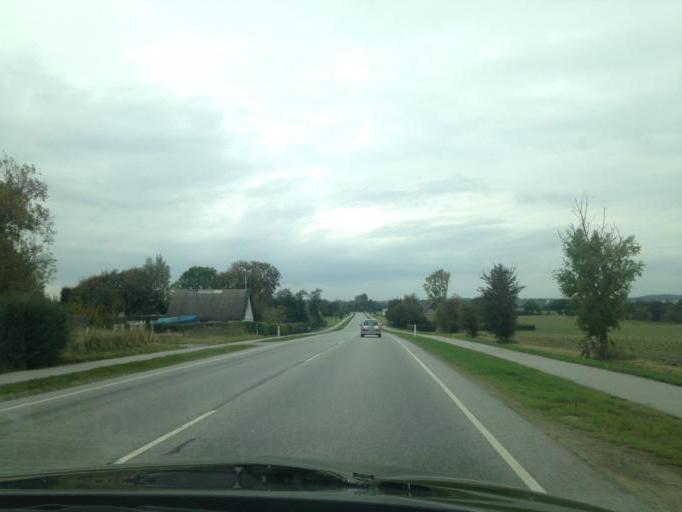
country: DK
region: South Denmark
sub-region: Kolding Kommune
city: Christiansfeld
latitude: 55.3360
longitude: 9.4899
